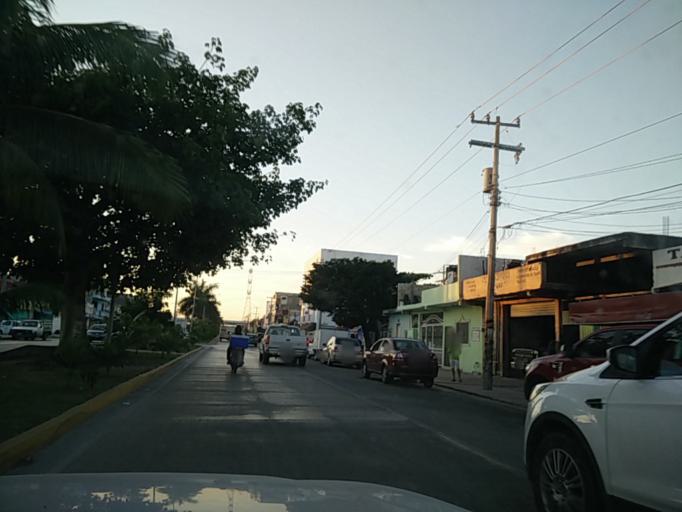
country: MX
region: Quintana Roo
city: Playa del Carmen
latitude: 20.6409
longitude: -87.0692
